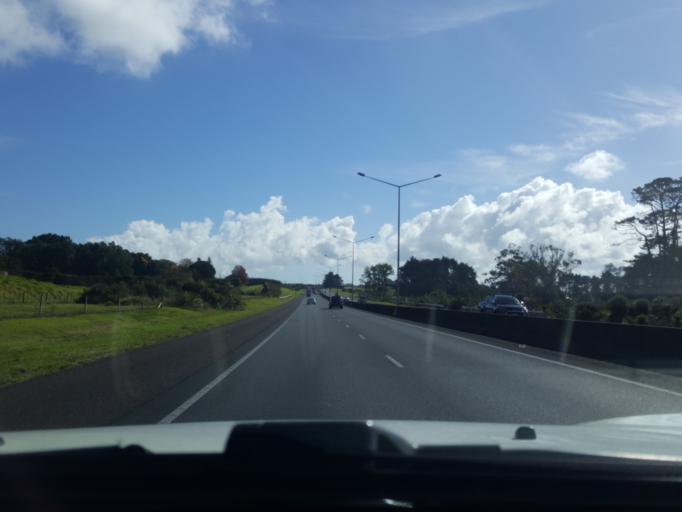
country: NZ
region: Auckland
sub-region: Auckland
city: Rosebank
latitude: -36.8019
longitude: 174.6023
